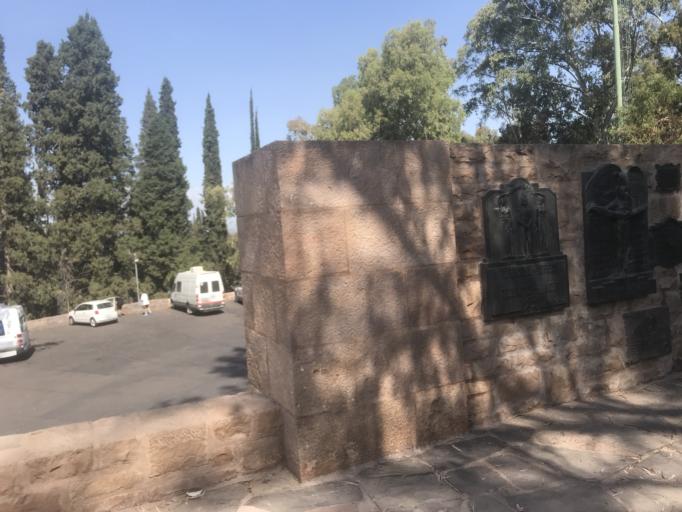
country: AR
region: Mendoza
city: Mendoza
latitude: -32.8871
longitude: -68.8906
